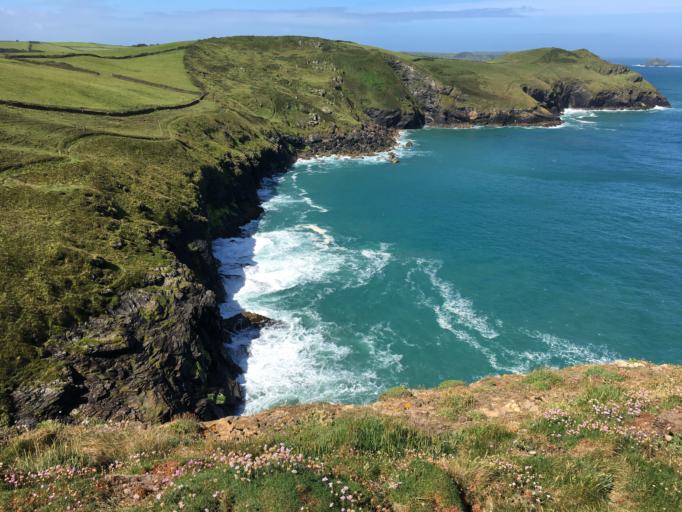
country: GB
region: England
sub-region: Cornwall
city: Polzeath
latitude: 50.5946
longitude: -4.8561
